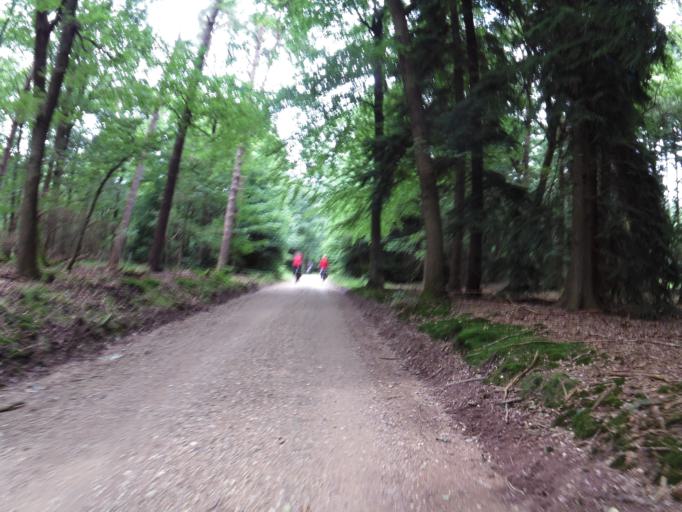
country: NL
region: Gelderland
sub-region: Gemeente Apeldoorn
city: Loenen
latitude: 52.1001
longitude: 6.0052
